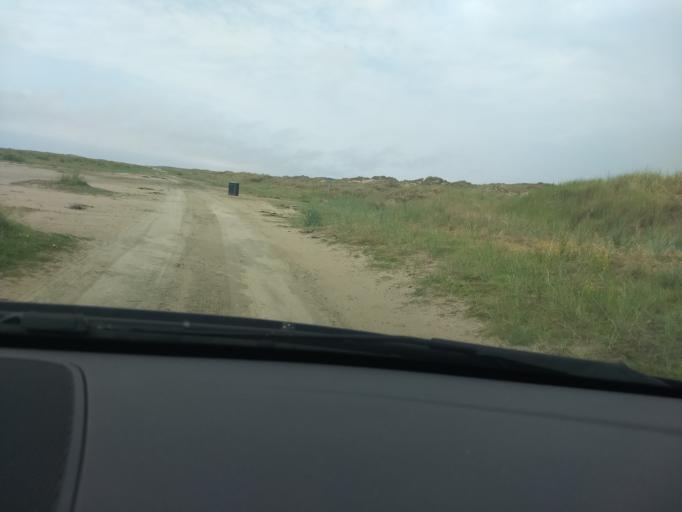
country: DK
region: South Denmark
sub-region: Fano Kommune
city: Nordby
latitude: 55.4058
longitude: 8.3888
